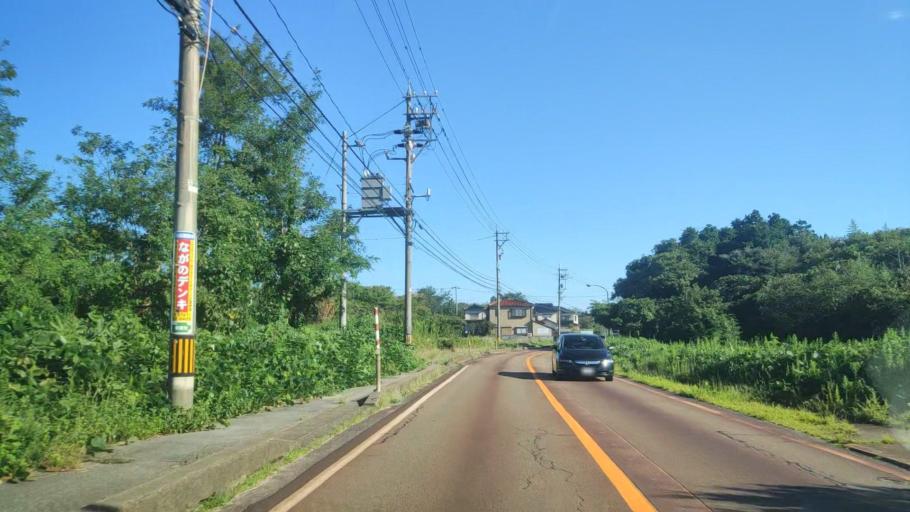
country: JP
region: Ishikawa
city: Hakui
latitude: 36.8749
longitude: 136.7735
